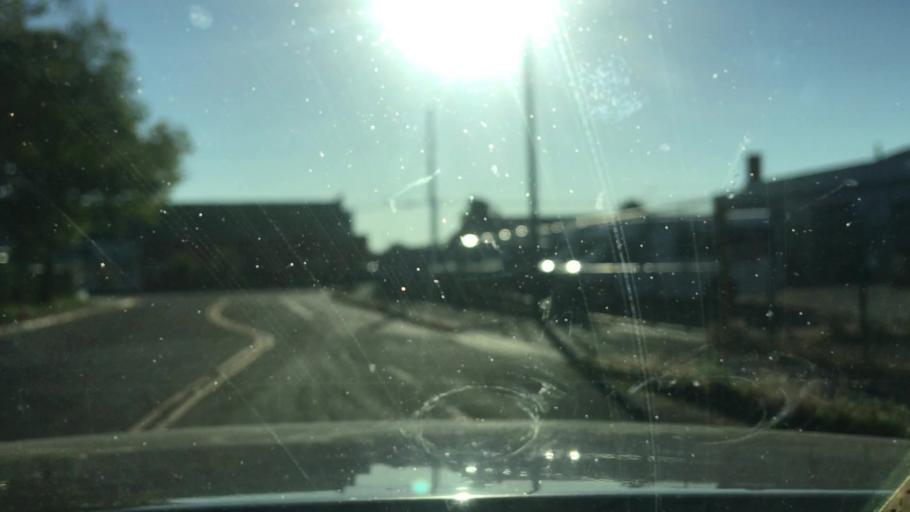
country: US
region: Oregon
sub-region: Lane County
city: Eugene
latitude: 44.0502
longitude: -123.1271
